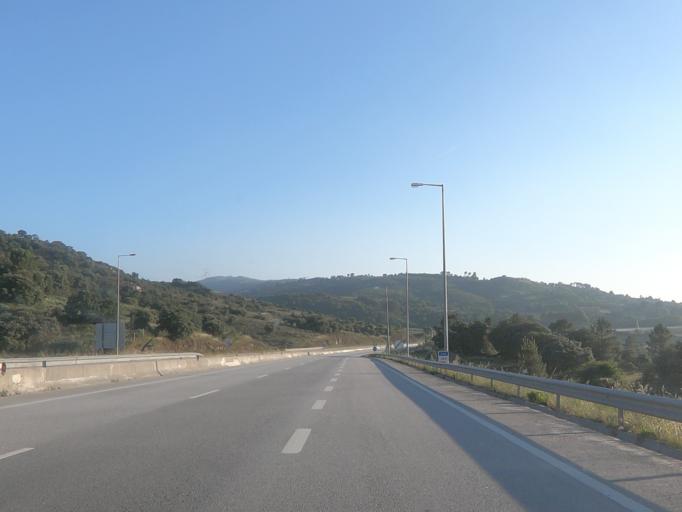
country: PT
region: Guarda
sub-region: Celorico da Beira
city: Celorico da Beira
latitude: 40.6288
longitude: -7.3587
